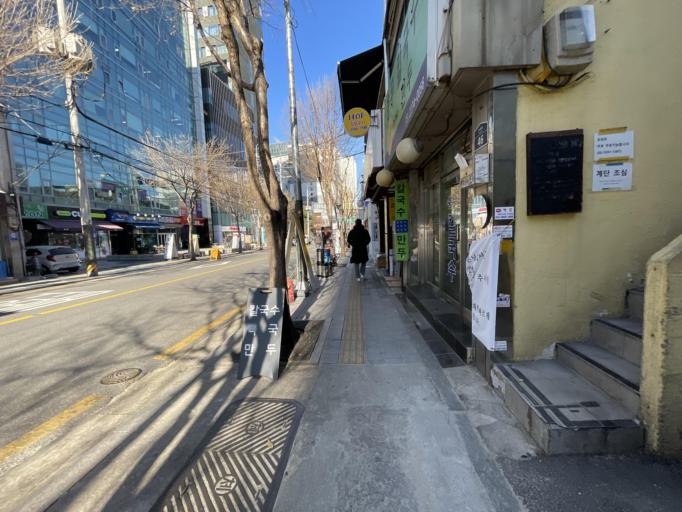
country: KR
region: Seoul
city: Seoul
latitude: 37.5651
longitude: 126.9900
